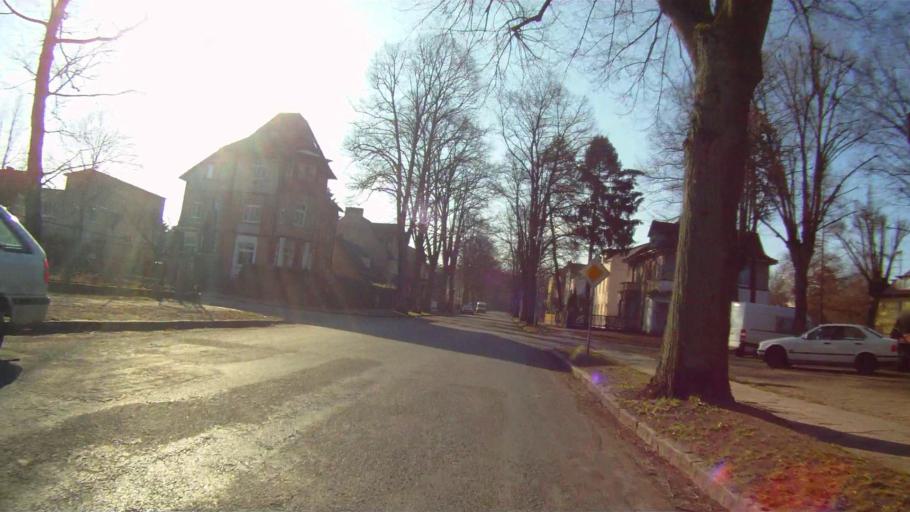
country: DE
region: Brandenburg
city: Schoneiche
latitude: 52.4574
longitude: 13.7026
